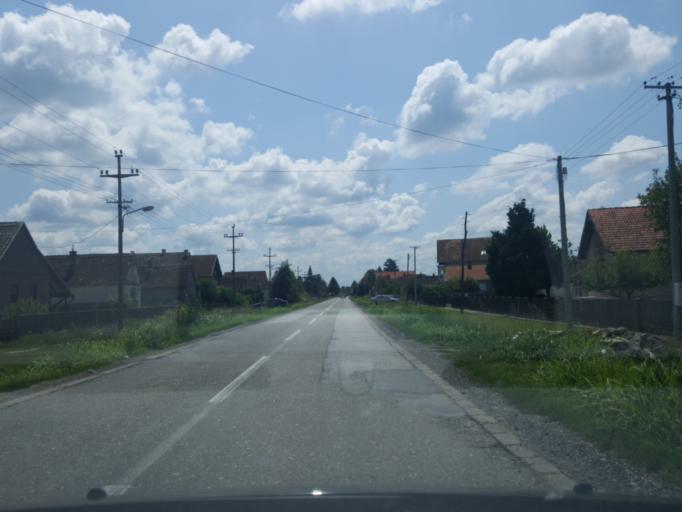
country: RS
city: Metkovic
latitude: 44.8583
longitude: 19.5456
